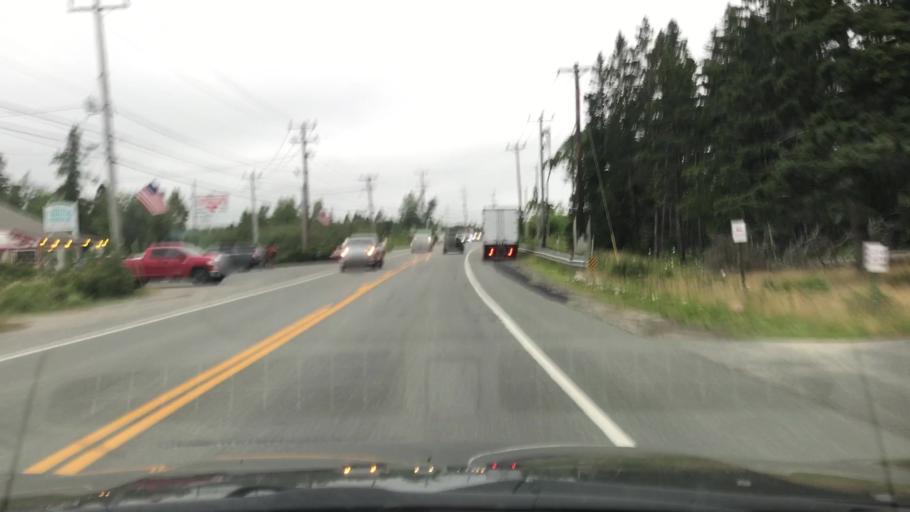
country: US
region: Maine
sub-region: Hancock County
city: Trenton
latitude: 44.4321
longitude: -68.3683
